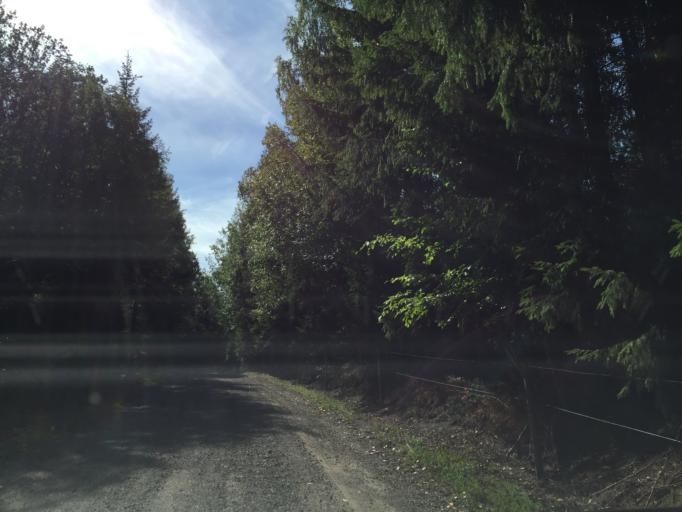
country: NO
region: Vestfold
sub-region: Hof
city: Hof
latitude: 59.4629
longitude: 10.1467
